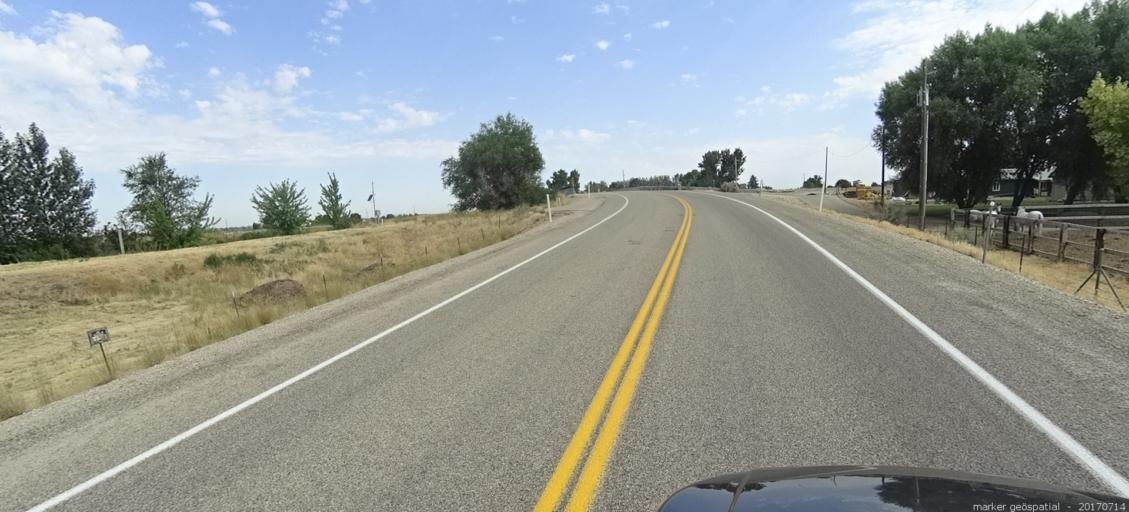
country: US
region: Idaho
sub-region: Ada County
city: Kuna
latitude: 43.4850
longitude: -116.3544
